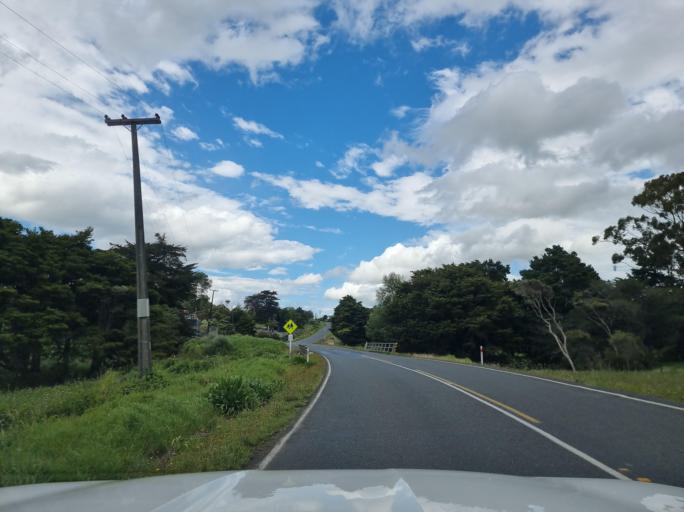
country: NZ
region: Northland
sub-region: Whangarei
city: Whangarei
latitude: -35.8461
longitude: 174.2836
